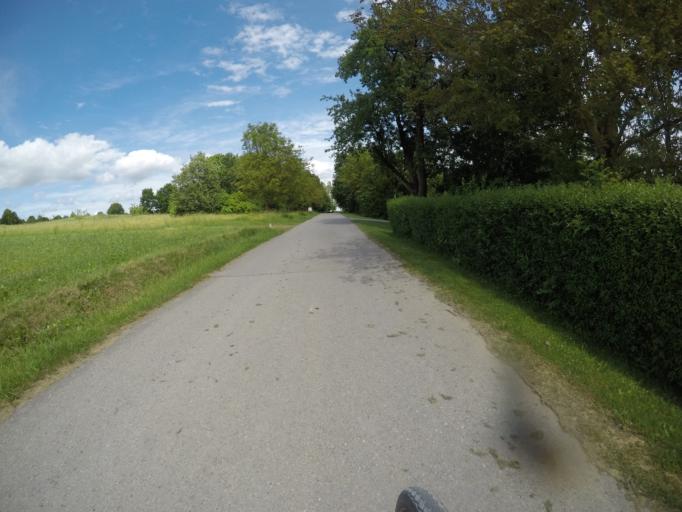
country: DE
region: Baden-Wuerttemberg
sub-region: Regierungsbezirk Stuttgart
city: Holzgerlingen
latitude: 48.6121
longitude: 9.0189
